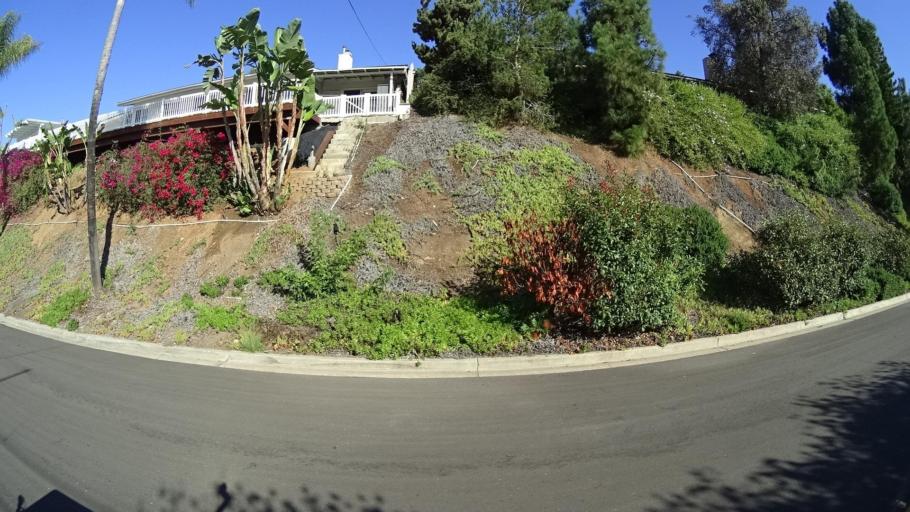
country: US
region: California
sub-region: San Diego County
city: Casa de Oro-Mount Helix
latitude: 32.7627
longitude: -116.9823
